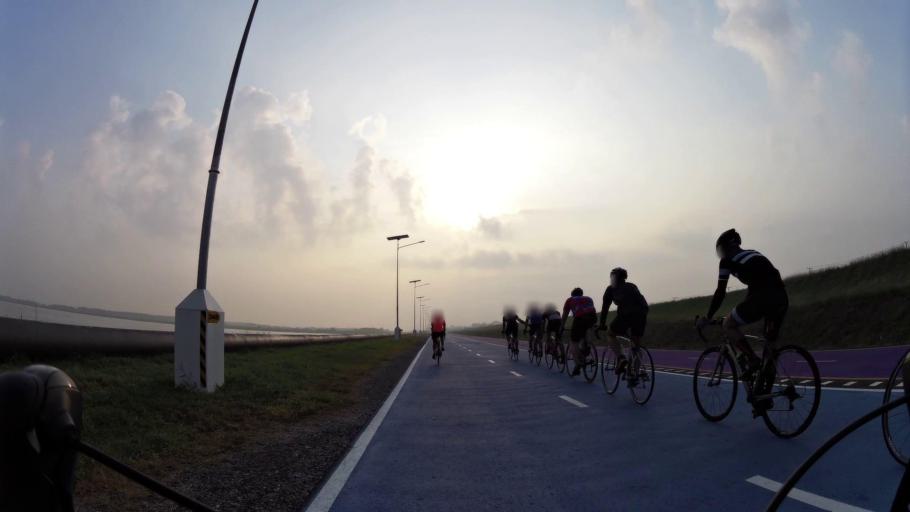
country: TH
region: Bangkok
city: Lat Krabang
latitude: 13.6968
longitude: 100.7750
